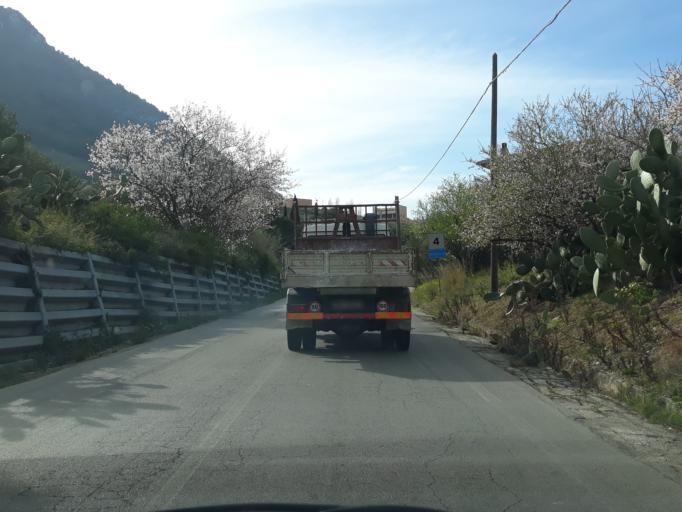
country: IT
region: Sicily
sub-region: Palermo
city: Piano Maglio-Blandino
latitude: 38.0398
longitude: 13.3203
